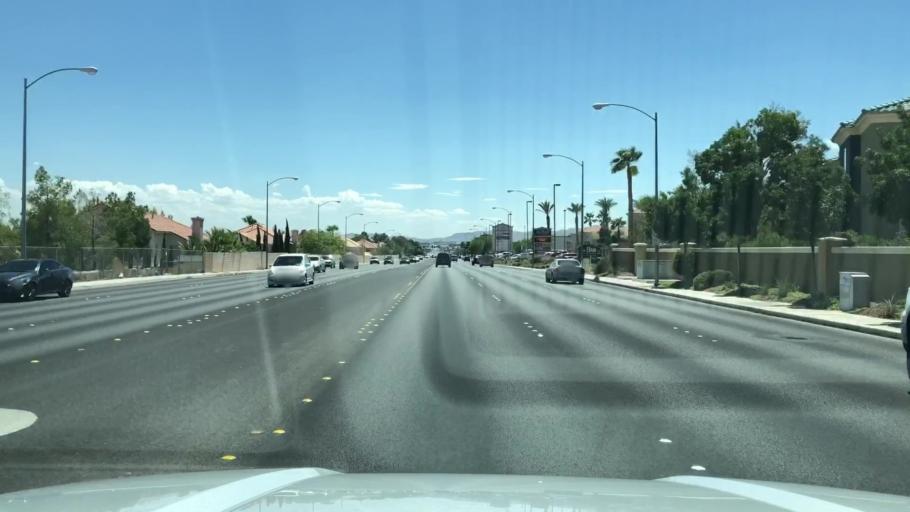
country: US
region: Nevada
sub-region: Clark County
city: Spring Valley
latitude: 36.1043
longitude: -115.2793
